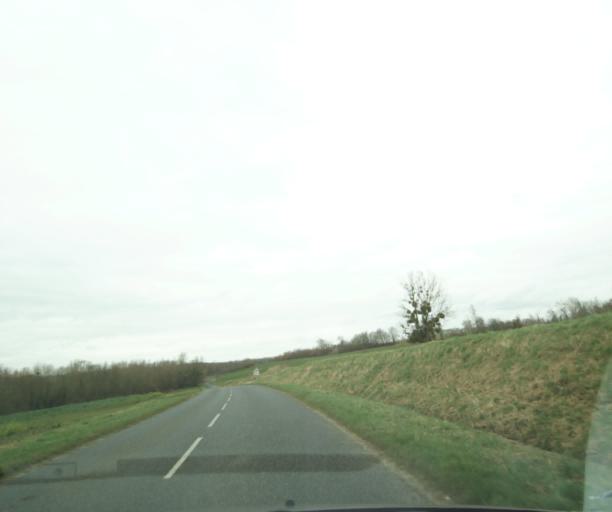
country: FR
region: Picardie
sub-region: Departement de l'Oise
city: Noyon
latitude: 49.5939
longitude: 2.9931
